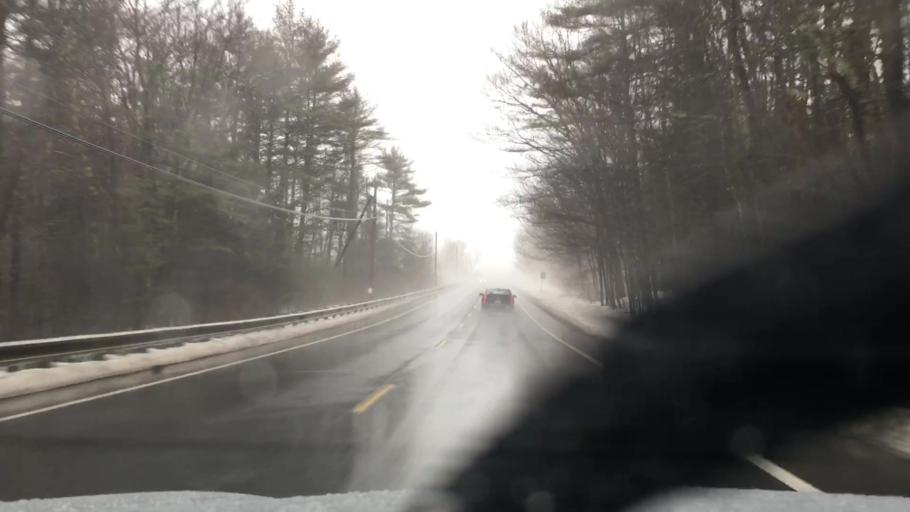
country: US
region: Massachusetts
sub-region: Franklin County
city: Orange
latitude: 42.5393
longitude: -72.3025
